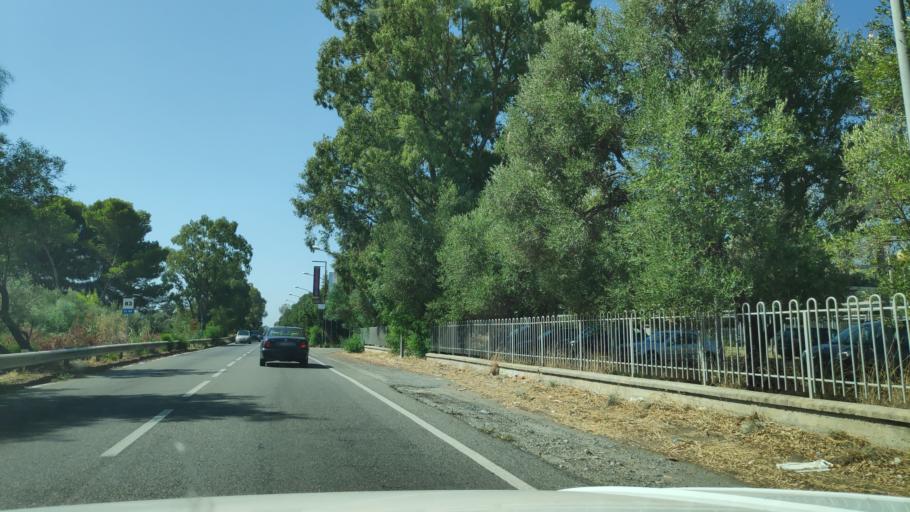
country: IT
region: Calabria
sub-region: Provincia di Reggio Calabria
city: Bianco
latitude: 38.1218
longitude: 16.1591
